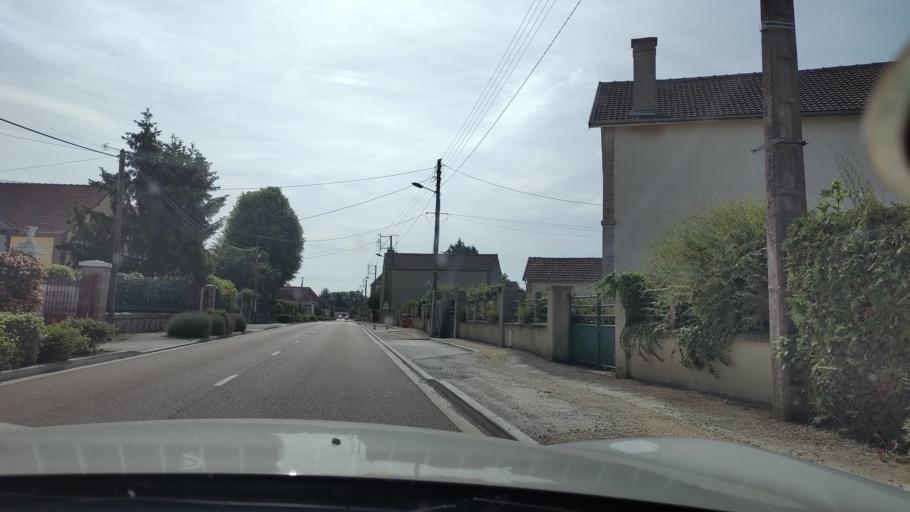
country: FR
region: Champagne-Ardenne
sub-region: Departement de l'Aube
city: Marigny-le-Chatel
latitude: 48.4049
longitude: 3.7264
